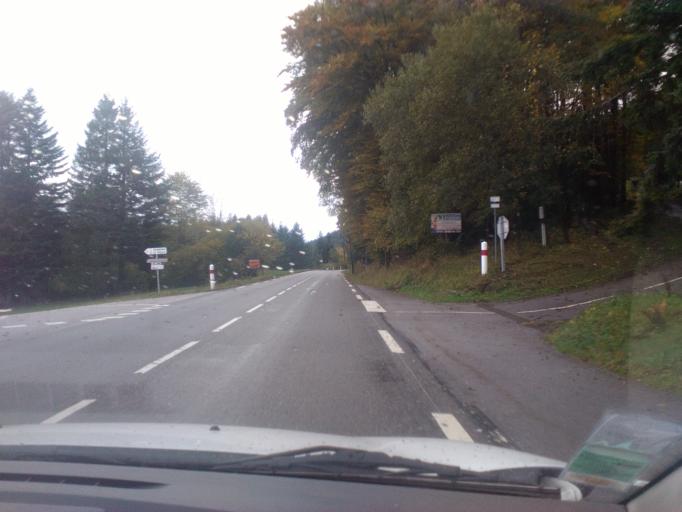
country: FR
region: Lorraine
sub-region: Departement des Vosges
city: Xonrupt-Longemer
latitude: 48.1218
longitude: 6.9123
